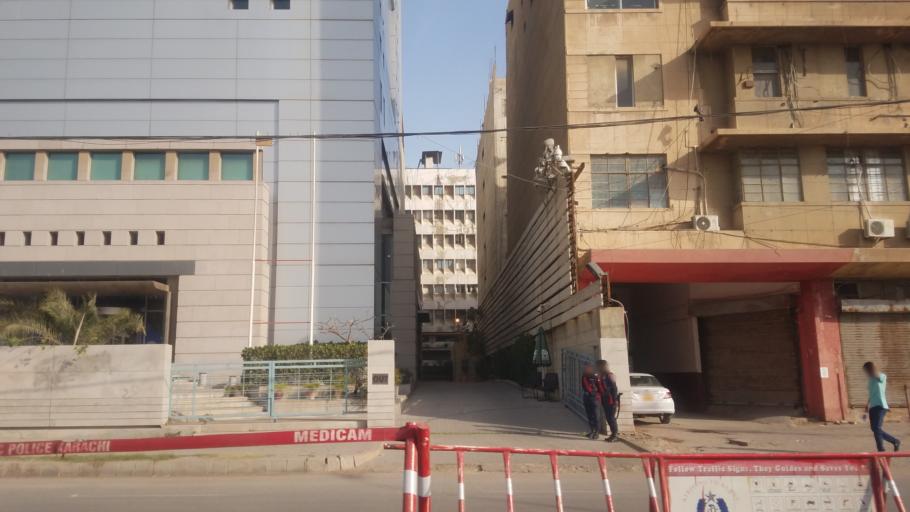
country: PK
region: Sindh
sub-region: Karachi District
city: Karachi
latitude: 24.8499
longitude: 67.0090
